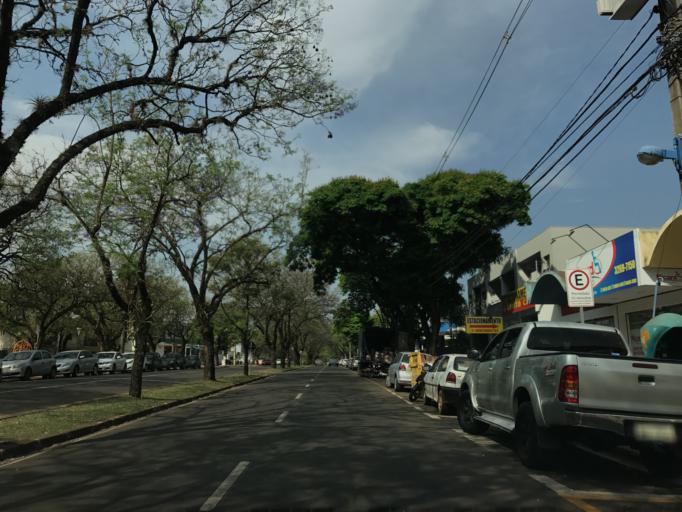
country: BR
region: Parana
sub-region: Maringa
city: Maringa
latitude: -23.4184
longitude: -51.9232
